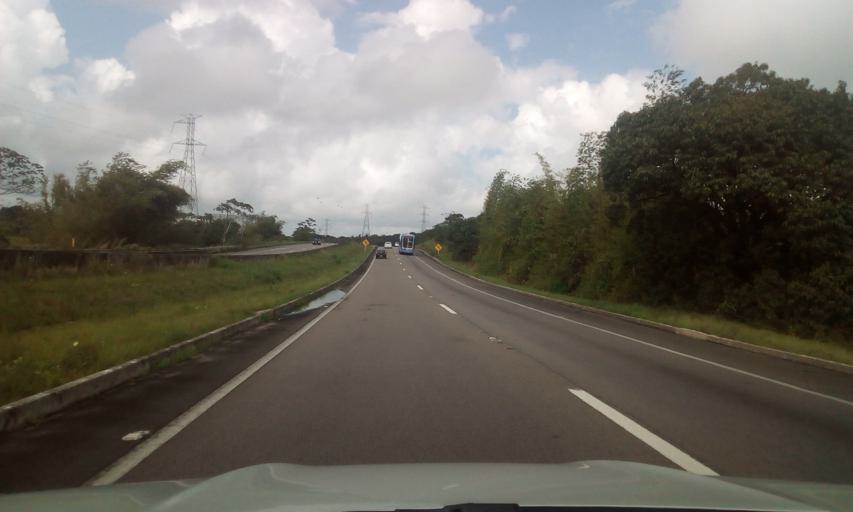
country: BR
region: Paraiba
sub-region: Conde
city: Conde
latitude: -7.3103
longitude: -34.9447
